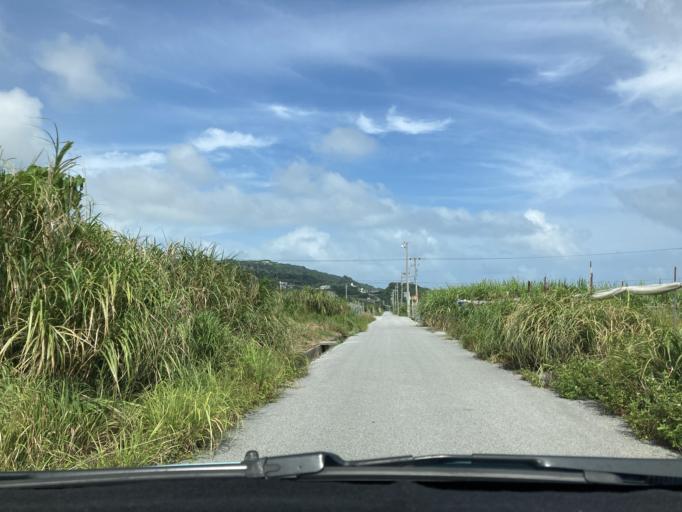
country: JP
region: Okinawa
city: Ginowan
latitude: 26.1493
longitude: 127.8038
